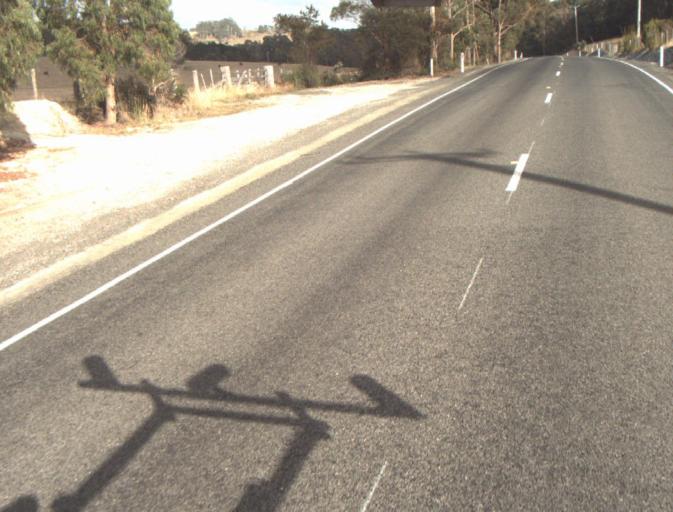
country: AU
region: Tasmania
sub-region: Dorset
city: Bridport
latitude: -41.1642
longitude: 147.2501
